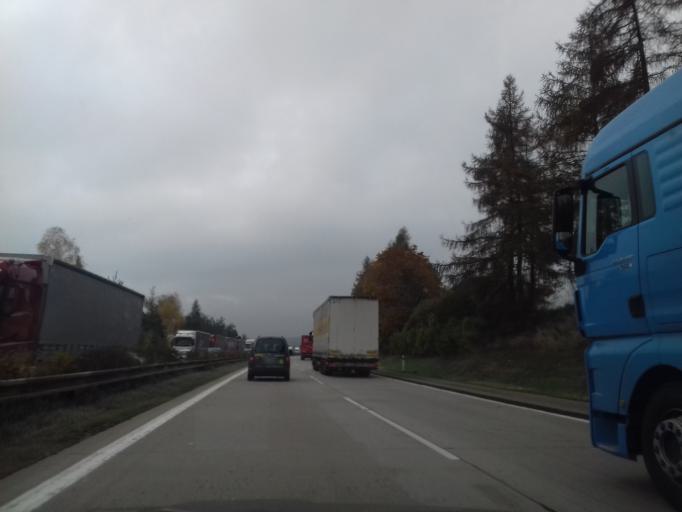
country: CZ
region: Vysocina
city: Luka nad Jihlavou
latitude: 49.4137
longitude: 15.7138
